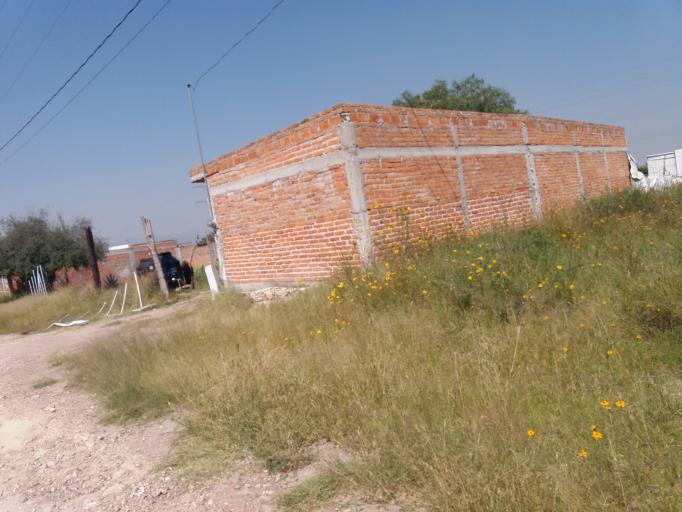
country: MX
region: Aguascalientes
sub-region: Aguascalientes
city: Penuelas (El Cienegal)
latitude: 21.7524
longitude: -102.2591
